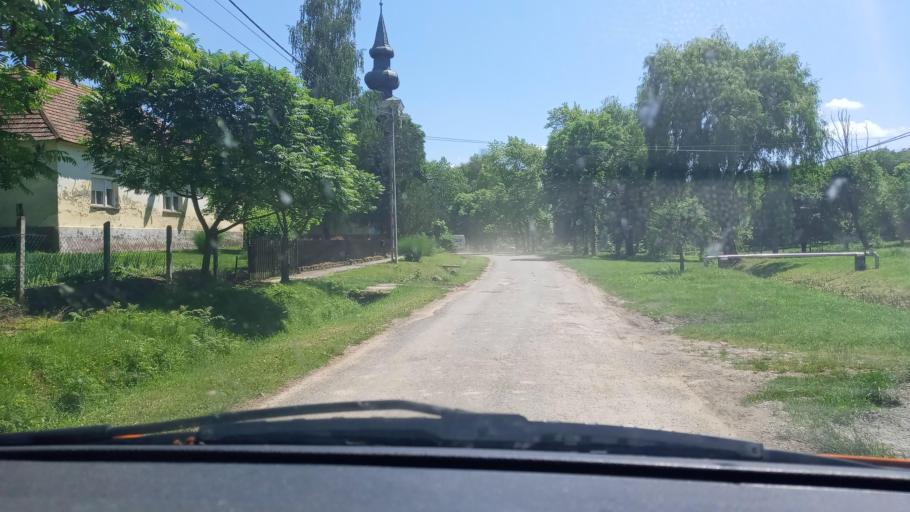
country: HU
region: Somogy
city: Kadarkut
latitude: 46.1830
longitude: 17.7244
